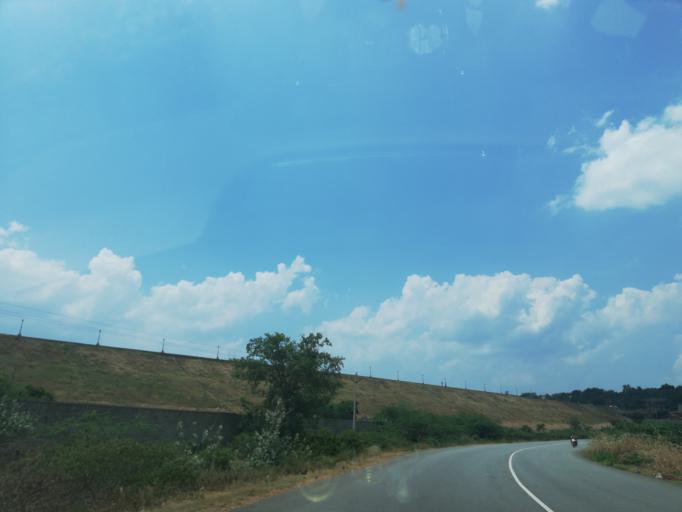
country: IN
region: Andhra Pradesh
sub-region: Guntur
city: Macherla
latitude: 16.5959
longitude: 79.3084
